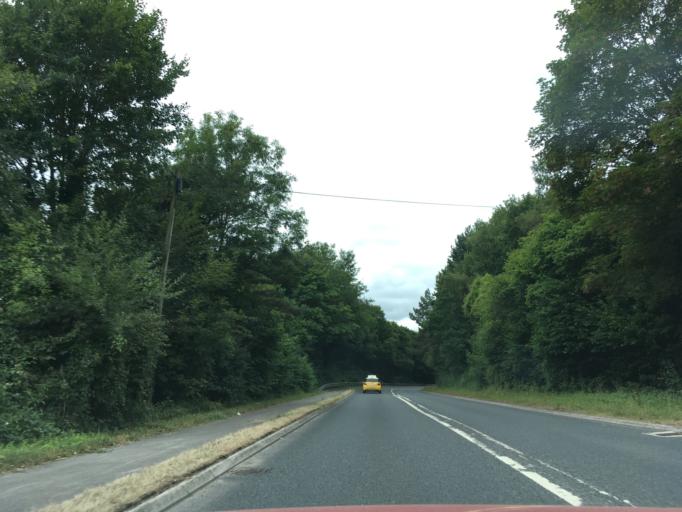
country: GB
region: Wales
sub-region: Monmouthshire
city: Gilwern
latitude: 51.8354
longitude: -3.0699
